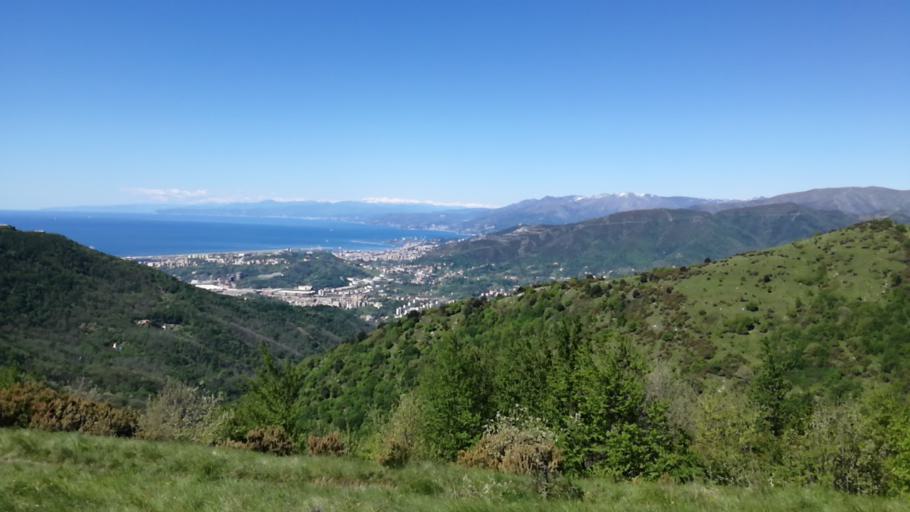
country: IT
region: Liguria
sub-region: Provincia di Genova
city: Manesseno
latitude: 44.4512
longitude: 8.9397
